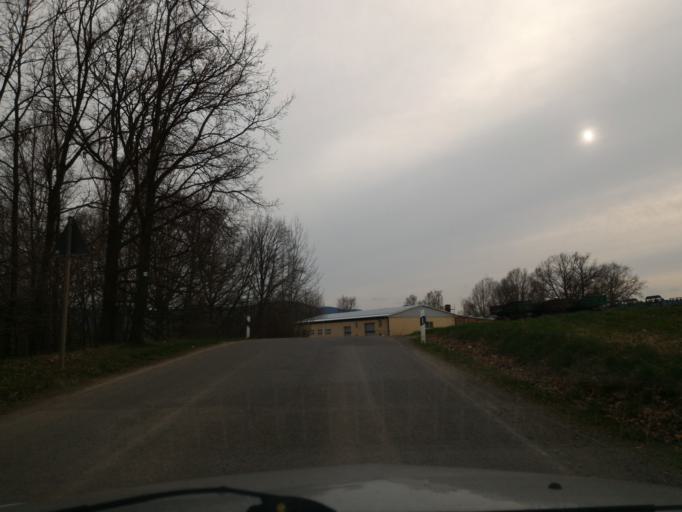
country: DE
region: Saxony
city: Grossschonau
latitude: 50.9034
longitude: 14.6907
